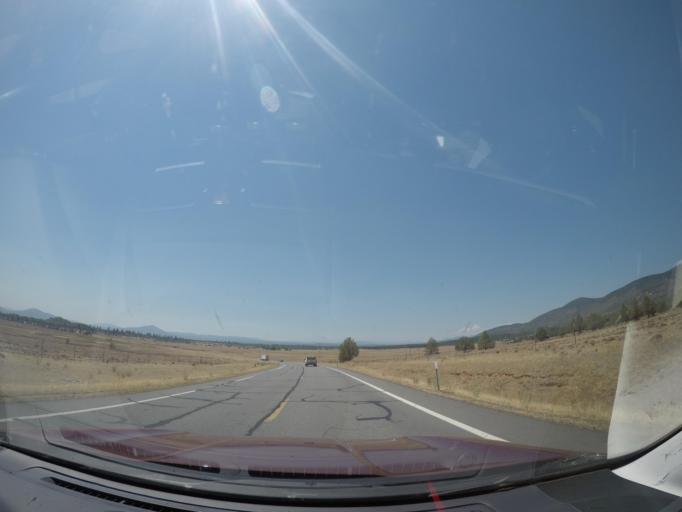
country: US
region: California
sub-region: Shasta County
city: Burney
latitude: 41.0988
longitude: -121.2895
